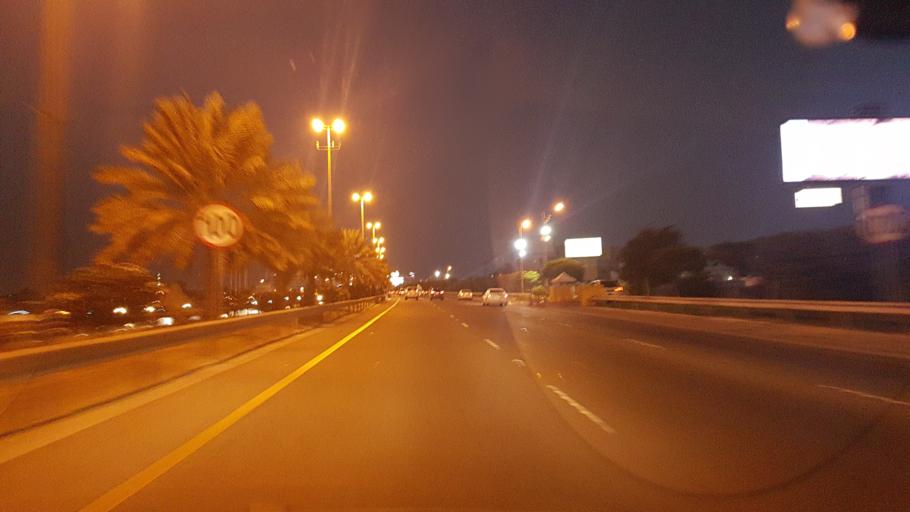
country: BH
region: Manama
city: Jidd Hafs
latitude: 26.2062
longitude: 50.5155
